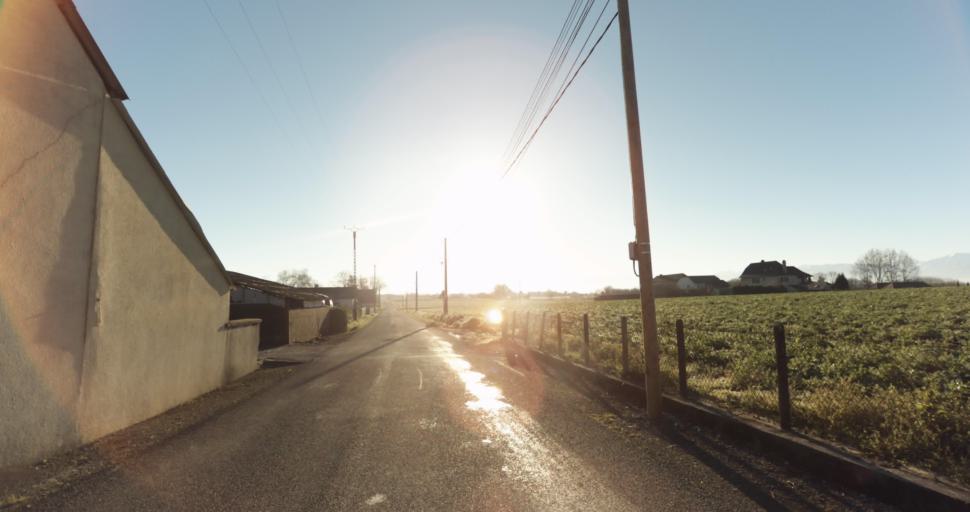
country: FR
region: Aquitaine
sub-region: Departement des Pyrenees-Atlantiques
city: Morlaas
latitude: 43.3222
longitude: -0.2518
